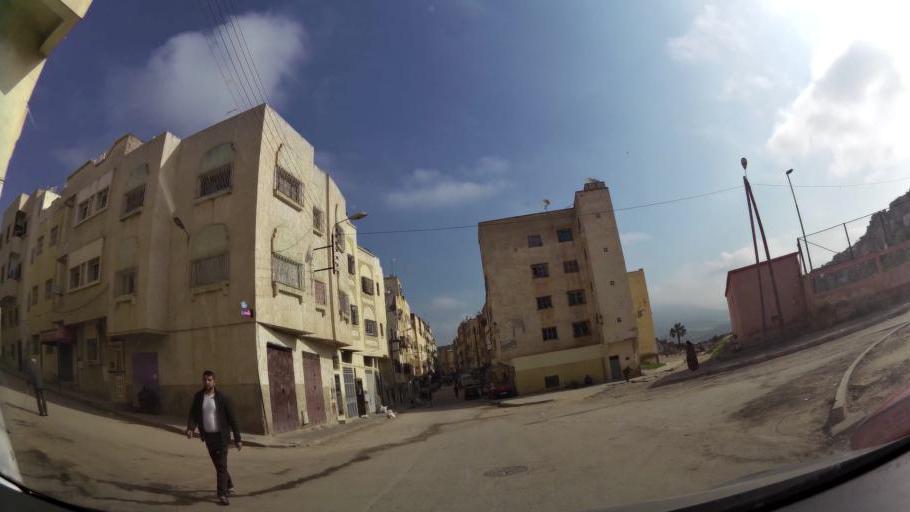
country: MA
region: Fes-Boulemane
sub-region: Fes
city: Fes
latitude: 34.0597
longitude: -4.9643
